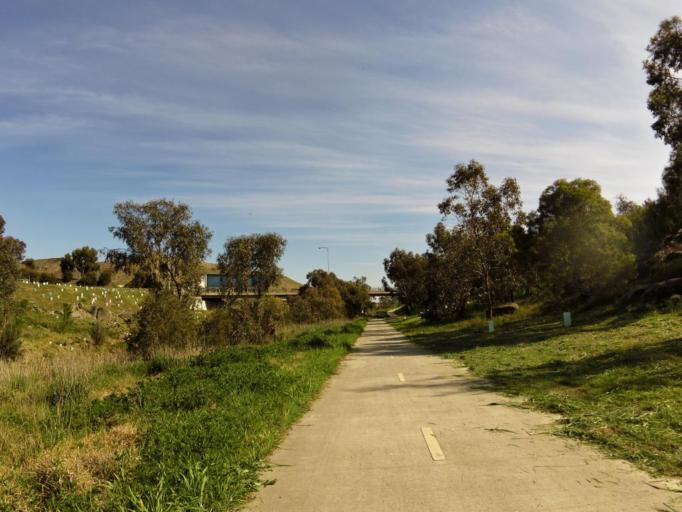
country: AU
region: Victoria
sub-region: Brimbank
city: Brooklyn
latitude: -37.8064
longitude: 144.8344
